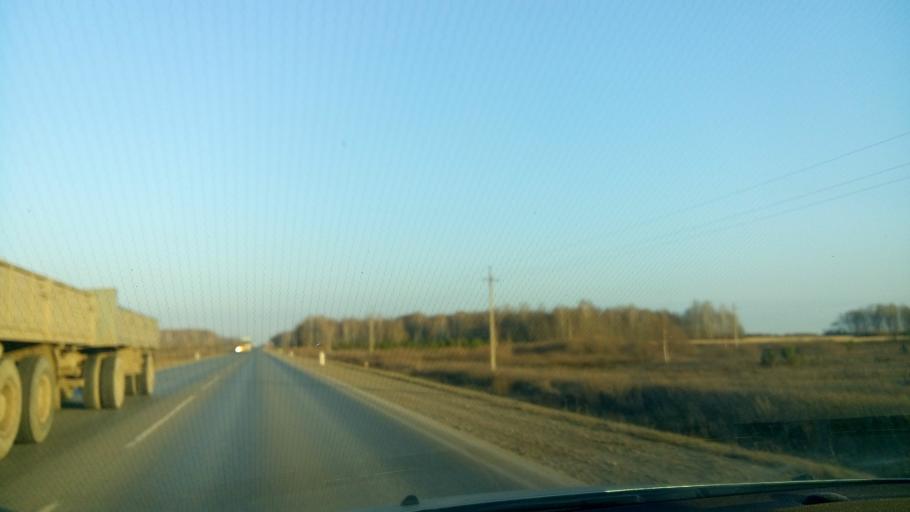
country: RU
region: Sverdlovsk
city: Bogdanovich
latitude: 56.7537
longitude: 62.1104
